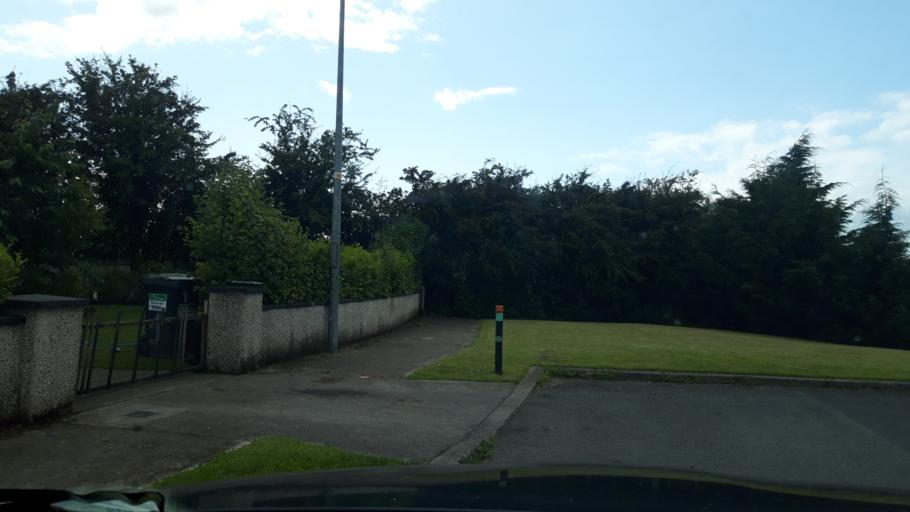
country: IE
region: Leinster
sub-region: Wicklow
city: Blessington
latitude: 53.1753
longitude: -6.5333
